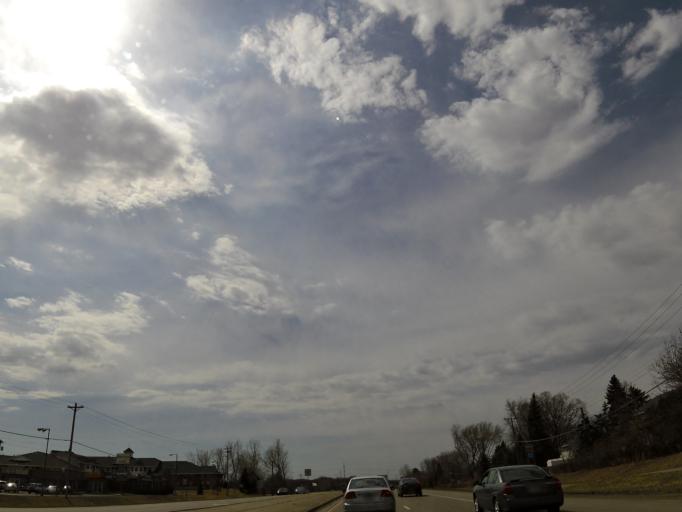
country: US
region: Minnesota
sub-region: Dakota County
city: Burnsville
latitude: 44.8049
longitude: -93.2290
